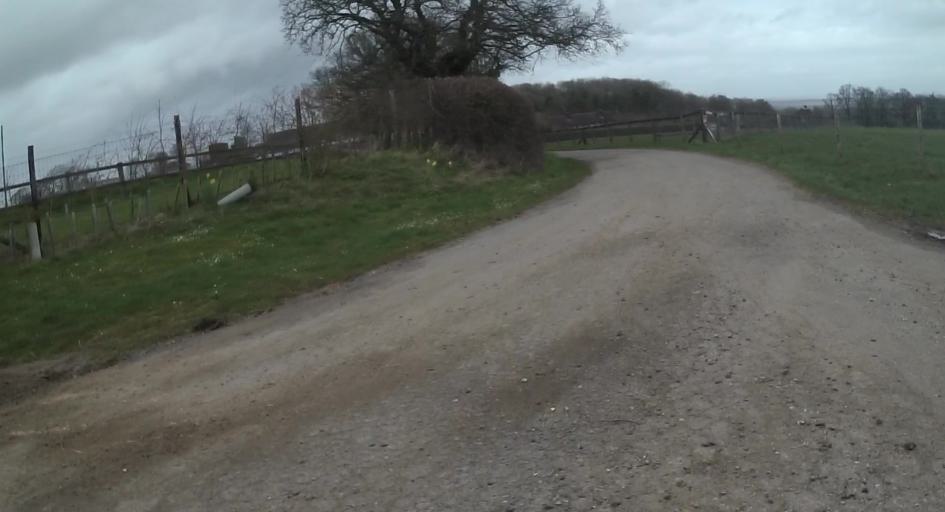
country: GB
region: England
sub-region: Hampshire
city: Kingsclere
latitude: 51.3096
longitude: -1.2192
